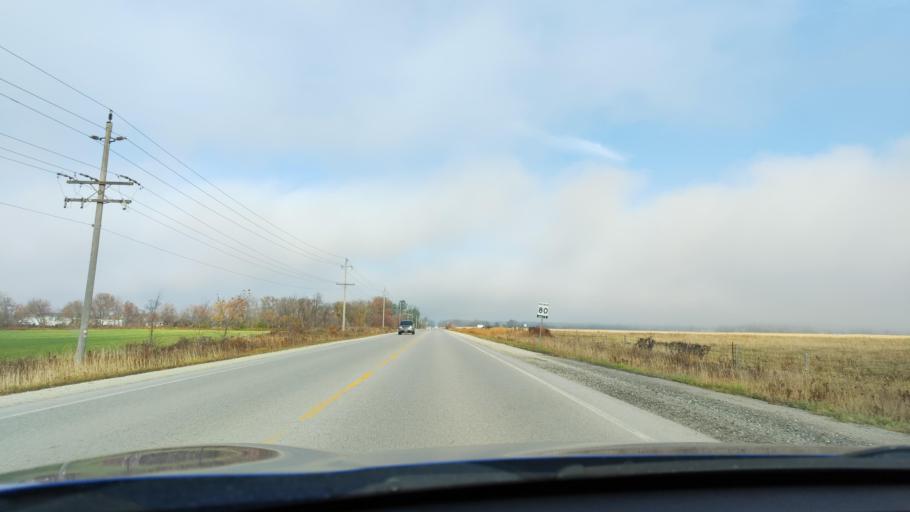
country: CA
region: Ontario
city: Wasaga Beach
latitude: 44.4448
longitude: -80.0685
